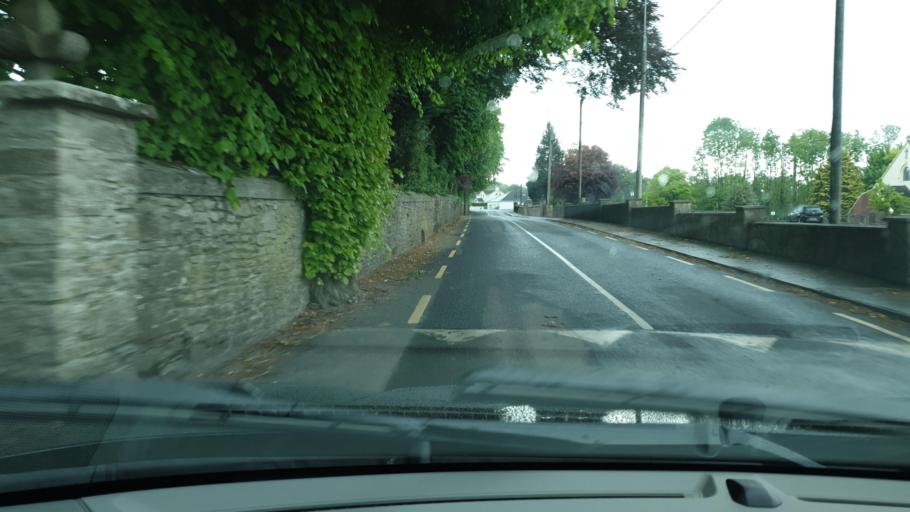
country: IE
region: Leinster
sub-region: Laois
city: Mountrath
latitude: 53.0560
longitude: -7.4080
